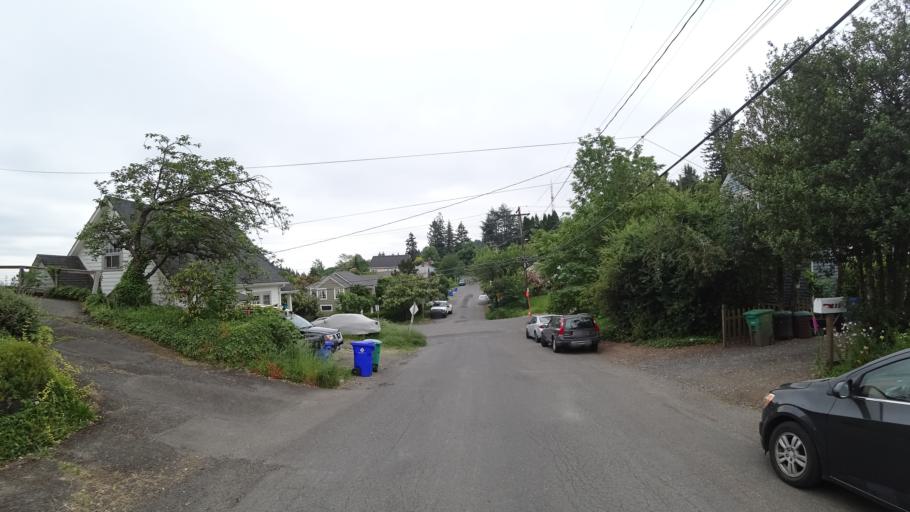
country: US
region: Oregon
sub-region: Multnomah County
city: Portland
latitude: 45.4994
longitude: -122.6923
